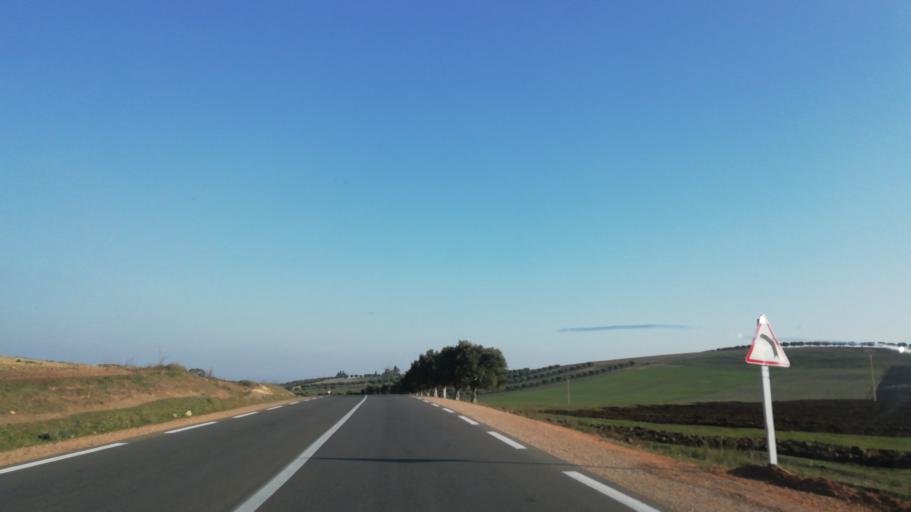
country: DZ
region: Ain Temouchent
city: Hammam Bou Hadjar
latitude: 35.1633
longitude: -0.8723
